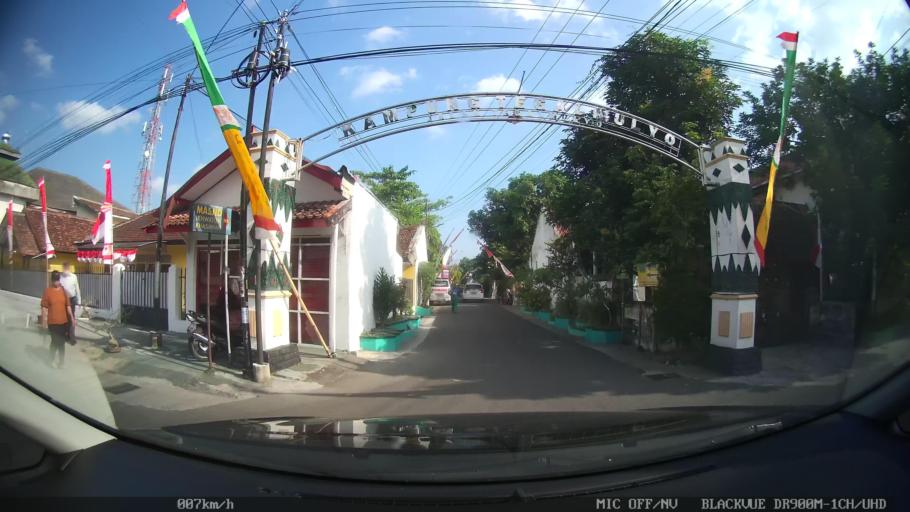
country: ID
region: Daerah Istimewa Yogyakarta
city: Yogyakarta
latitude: -7.7924
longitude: 110.3525
